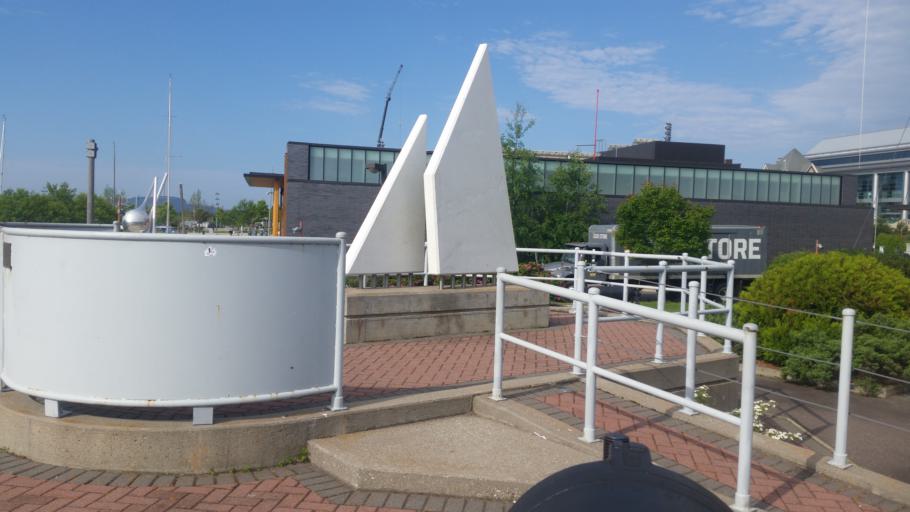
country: CA
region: Ontario
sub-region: Thunder Bay District
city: Thunder Bay
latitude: 48.4342
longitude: -89.2161
